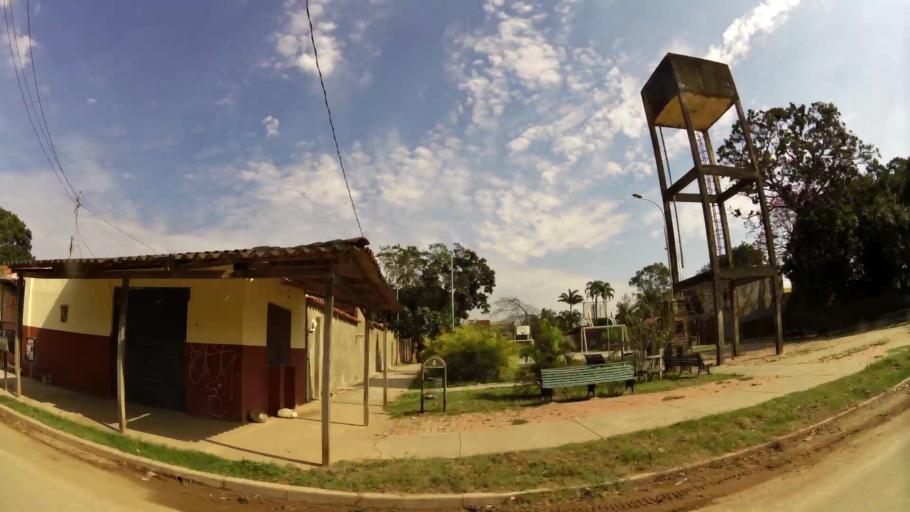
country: BO
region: Santa Cruz
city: Santa Cruz de la Sierra
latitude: -17.7305
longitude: -63.1482
